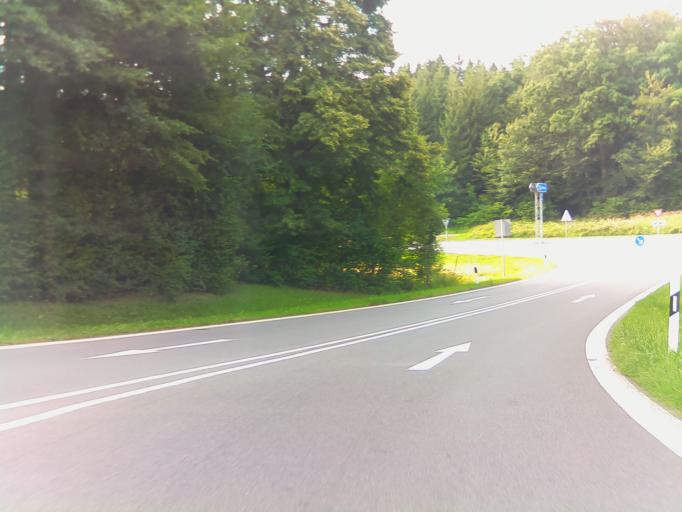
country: DE
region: Baden-Wuerttemberg
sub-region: Regierungsbezirk Stuttgart
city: Buch am Ahorn
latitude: 49.5378
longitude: 9.5830
